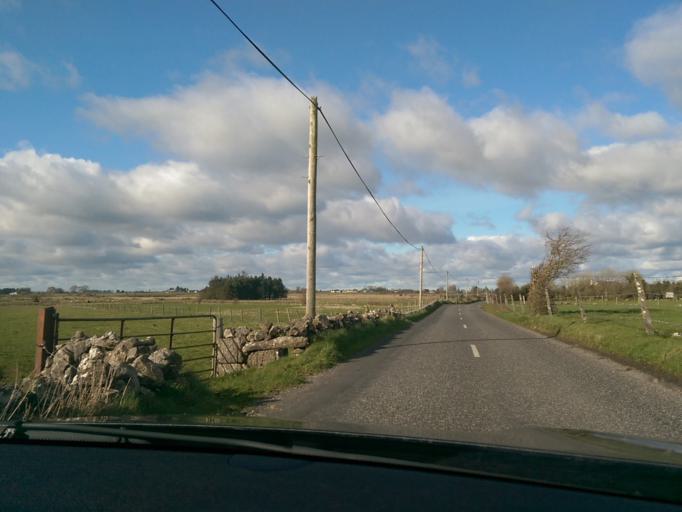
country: IE
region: Connaught
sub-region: County Galway
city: Athenry
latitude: 53.4294
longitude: -8.5727
